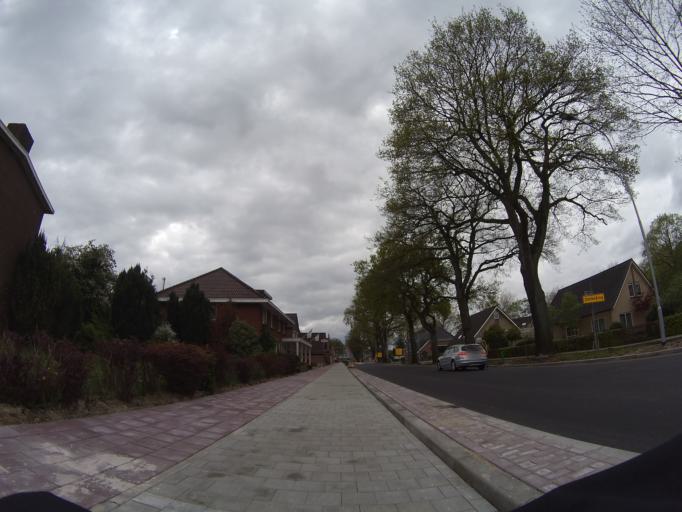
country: NL
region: Drenthe
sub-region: Gemeente Emmen
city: Emmen
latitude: 52.7941
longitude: 6.8990
